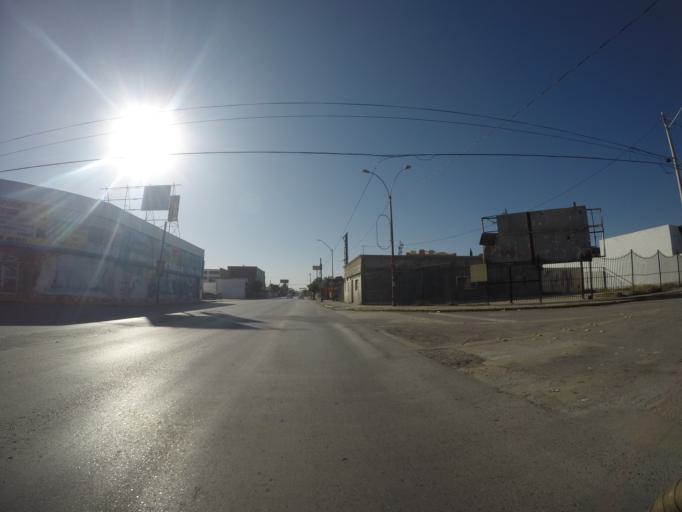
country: MX
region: Chihuahua
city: Ciudad Juarez
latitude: 31.7379
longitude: -106.4621
